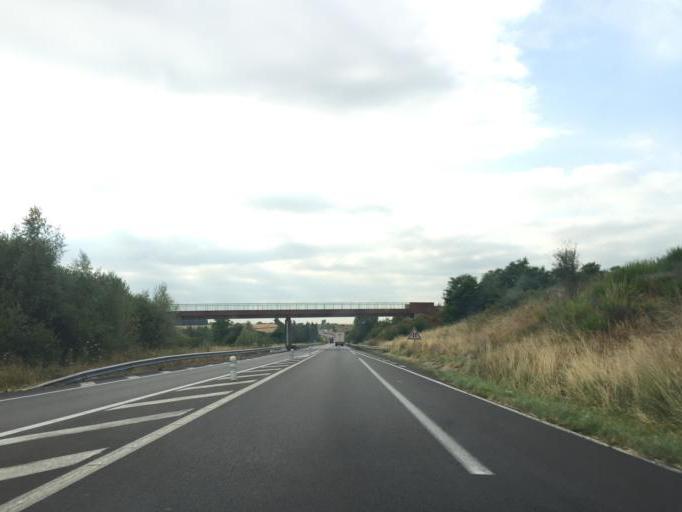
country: FR
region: Auvergne
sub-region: Departement de l'Allier
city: Saint-Francois
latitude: 46.4680
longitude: 3.8784
